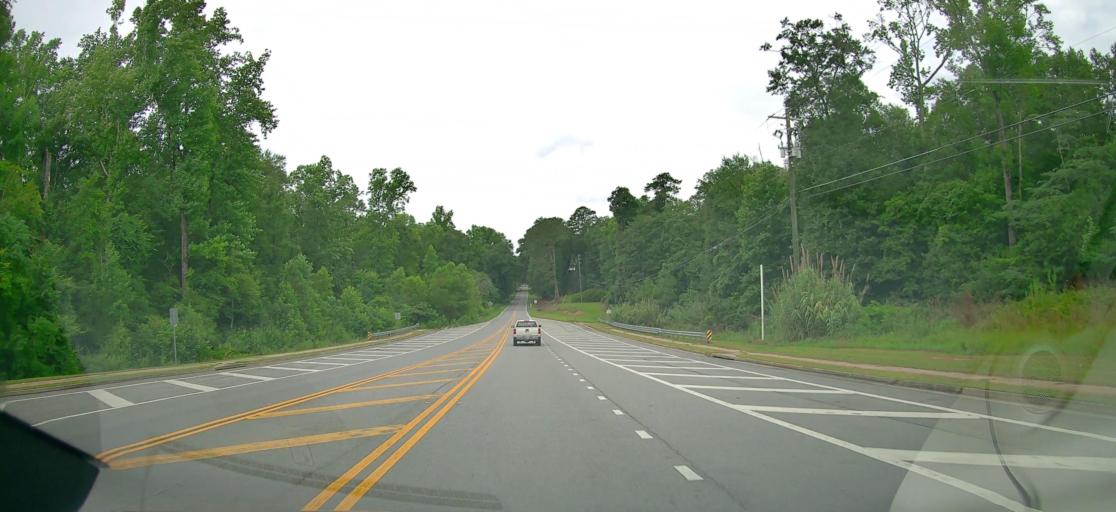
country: US
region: Georgia
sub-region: Peach County
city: Byron
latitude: 32.7168
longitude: -83.7362
